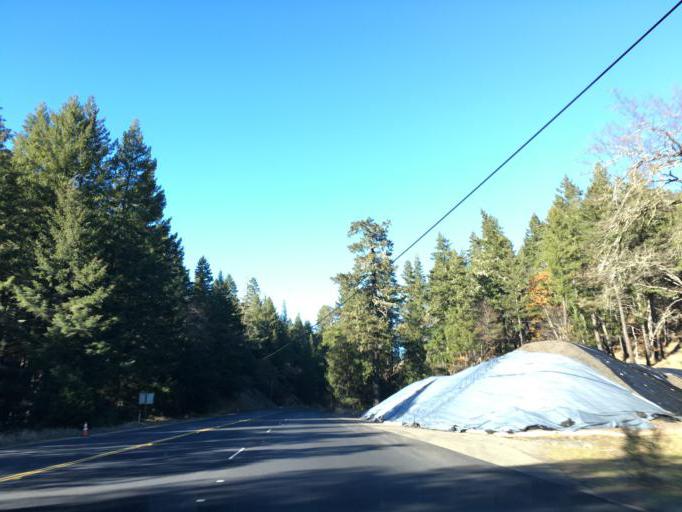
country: US
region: California
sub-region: Mendocino County
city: Laytonville
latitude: 39.7841
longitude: -123.5438
